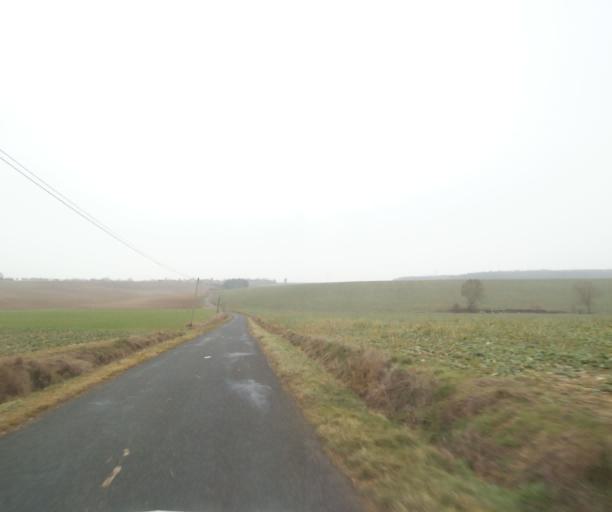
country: FR
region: Champagne-Ardenne
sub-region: Departement de la Haute-Marne
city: Bienville
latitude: 48.5088
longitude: 5.0211
